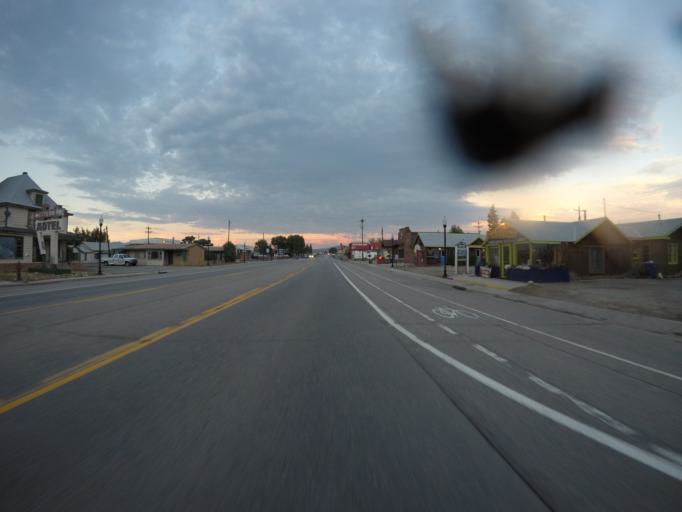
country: US
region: Colorado
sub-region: Grand County
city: Kremmling
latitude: 40.0590
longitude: -106.3958
